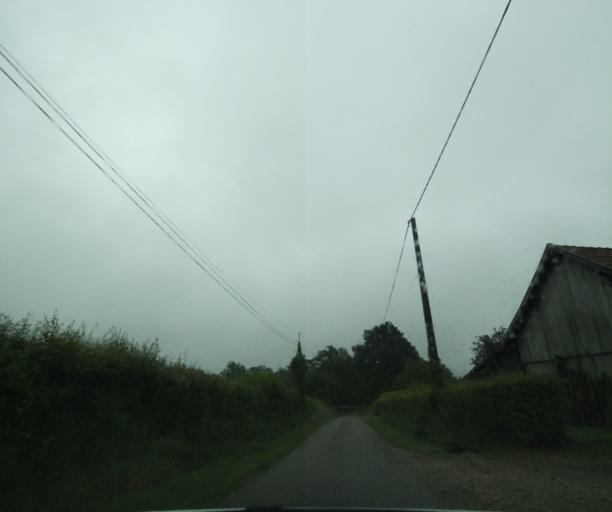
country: FR
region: Bourgogne
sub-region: Departement de Saone-et-Loire
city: Paray-le-Monial
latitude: 46.4127
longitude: 4.1886
